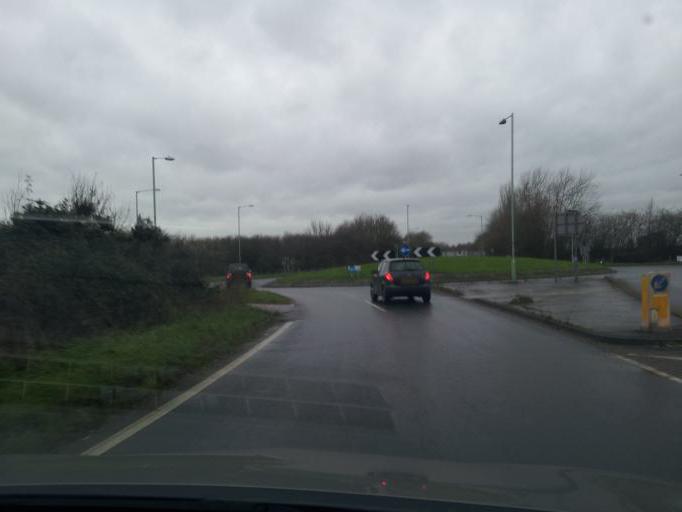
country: GB
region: England
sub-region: Norfolk
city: Diss
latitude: 52.3622
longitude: 1.1330
